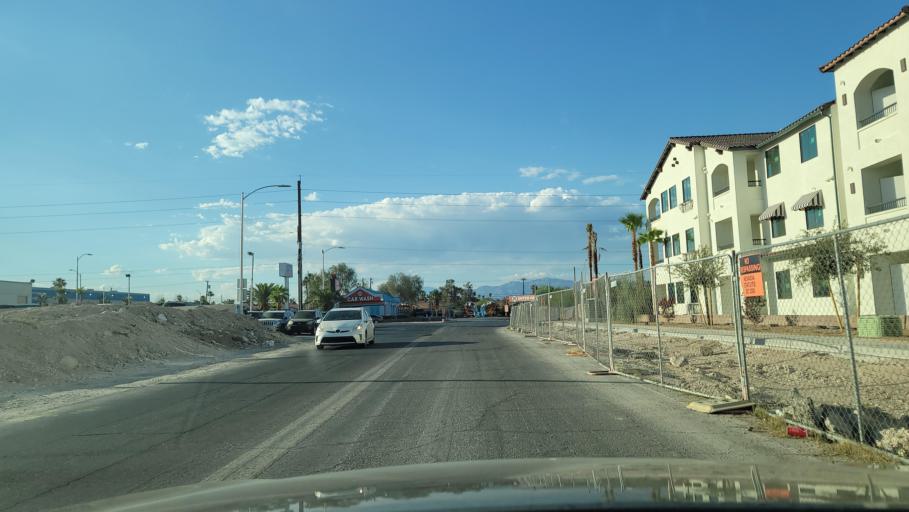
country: US
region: Nevada
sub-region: Clark County
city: Spring Valley
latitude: 36.1583
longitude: -115.2168
